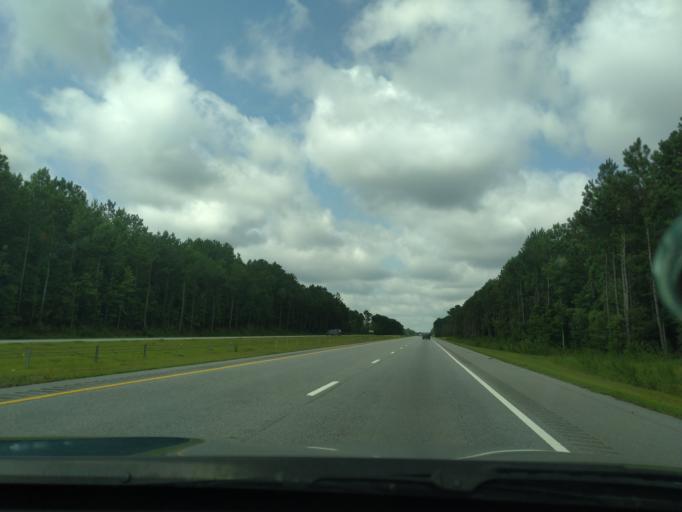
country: US
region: North Carolina
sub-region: Martin County
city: Williamston
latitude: 35.8279
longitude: -77.1381
